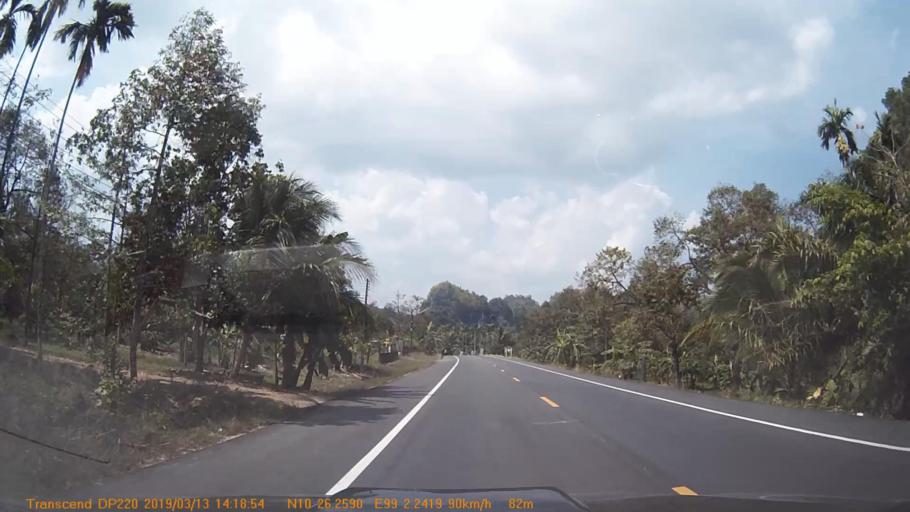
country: TH
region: Chumphon
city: Chumphon
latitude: 10.4263
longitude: 99.0407
